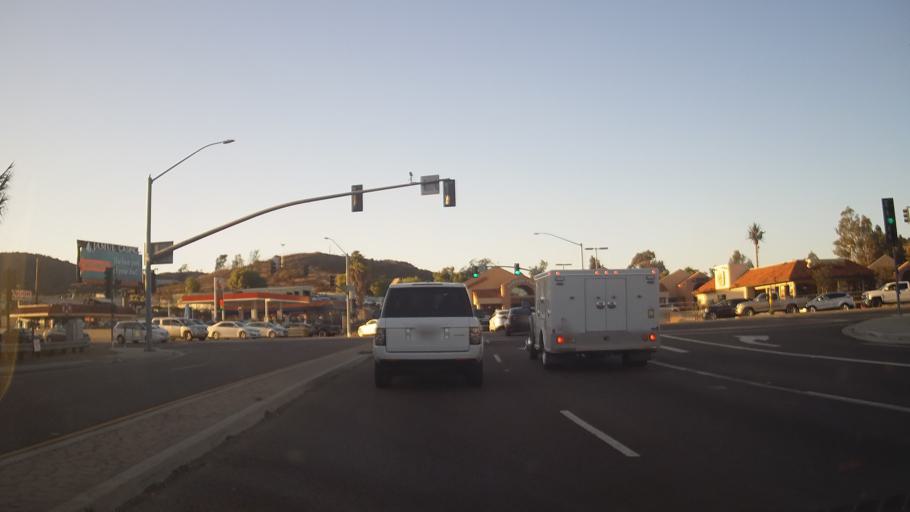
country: US
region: California
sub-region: San Diego County
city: Rancho San Diego
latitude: 32.7390
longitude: -116.9423
